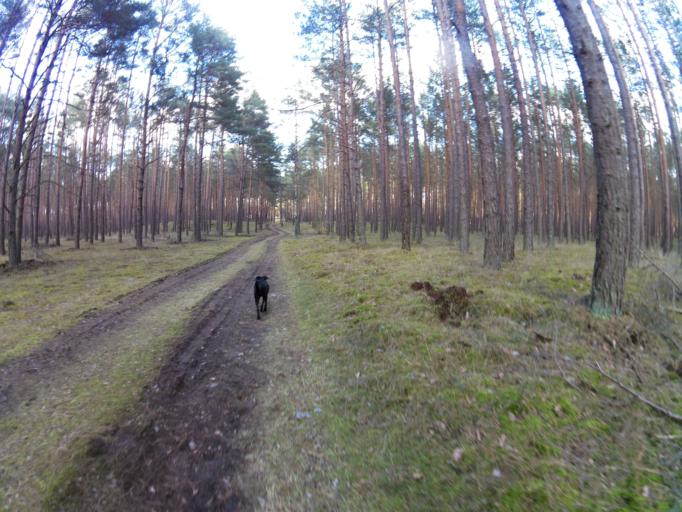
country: PL
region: West Pomeranian Voivodeship
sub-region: Powiat mysliborski
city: Debno
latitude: 52.7847
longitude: 14.7426
